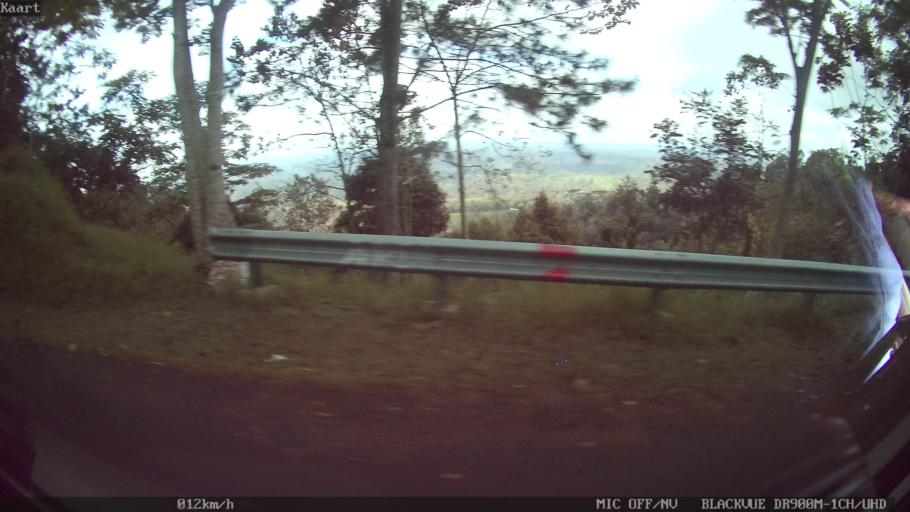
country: ID
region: Bali
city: Peneng
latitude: -8.3658
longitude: 115.2125
